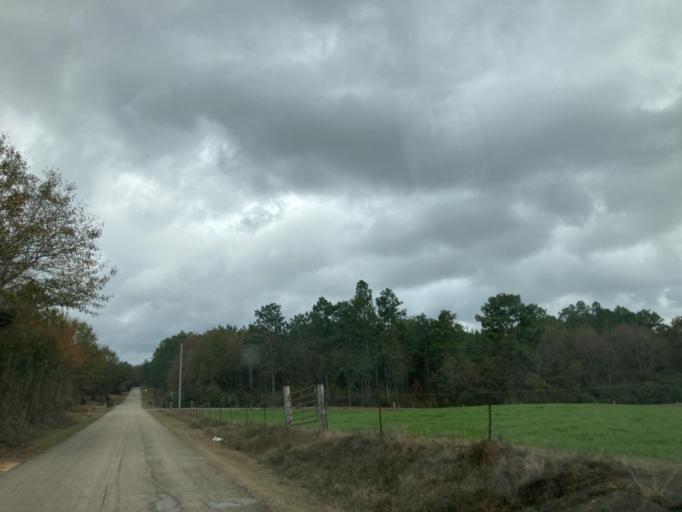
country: US
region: Mississippi
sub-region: Lamar County
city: Purvis
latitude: 31.1043
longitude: -89.5124
